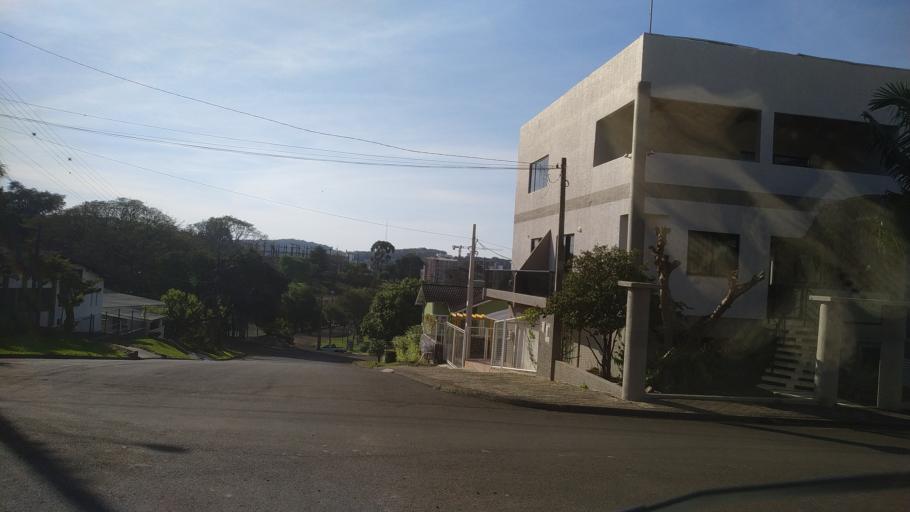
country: BR
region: Santa Catarina
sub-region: Chapeco
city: Chapeco
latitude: -27.0816
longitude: -52.6175
